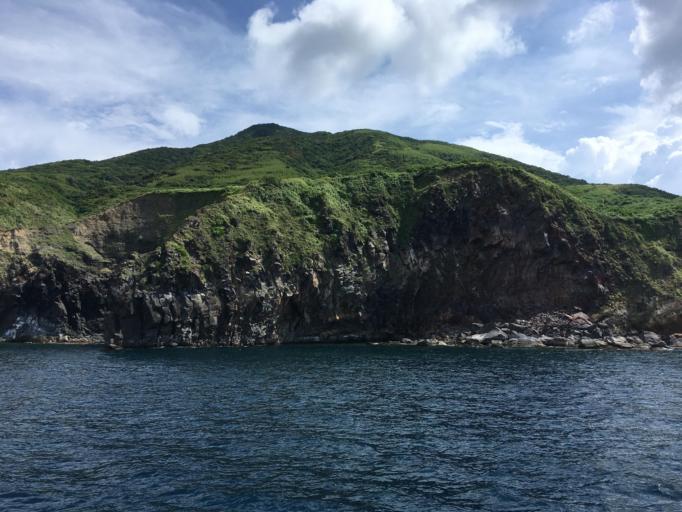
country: TW
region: Taiwan
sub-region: Yilan
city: Yilan
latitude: 24.8519
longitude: 121.9510
